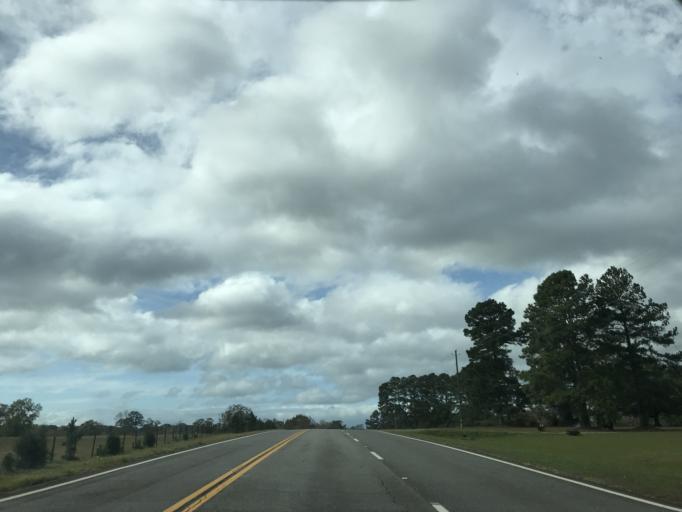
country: US
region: Georgia
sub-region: Jones County
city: Gray
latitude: 32.9711
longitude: -83.4934
